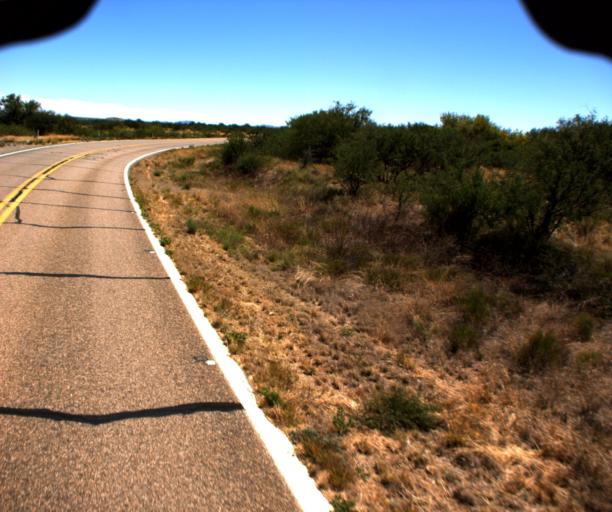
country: US
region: Arizona
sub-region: Pima County
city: Arivaca Junction
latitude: 31.6669
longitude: -111.4878
